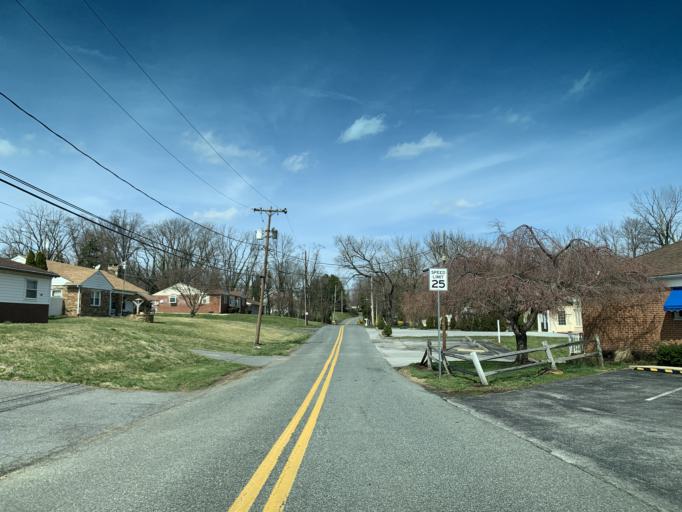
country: US
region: Delaware
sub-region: New Castle County
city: Newport
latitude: 39.7354
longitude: -75.6358
